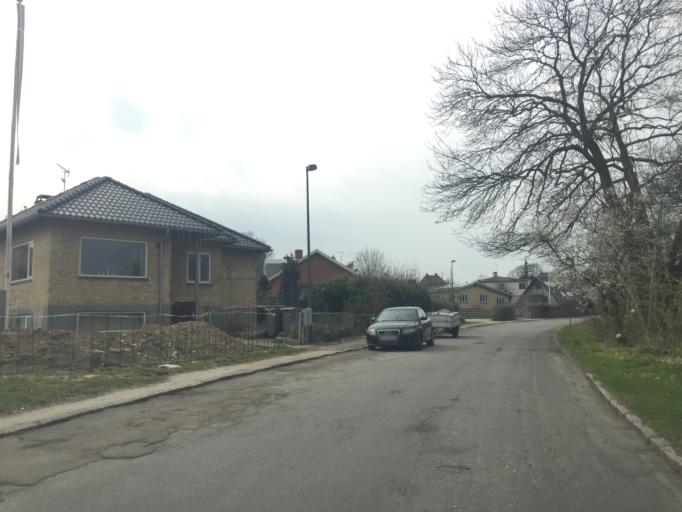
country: DK
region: Capital Region
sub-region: Kobenhavn
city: Vanlose
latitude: 55.7091
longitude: 12.4882
